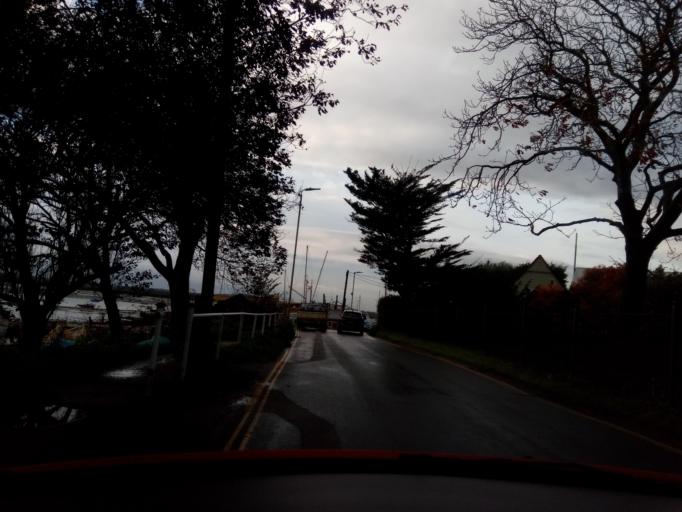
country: GB
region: England
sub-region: Essex
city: West Mersea
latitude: 51.7777
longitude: 0.8995
